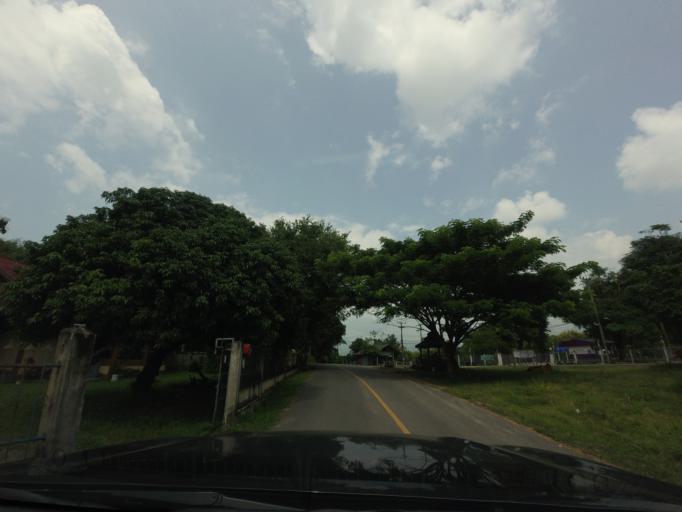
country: TH
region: Nan
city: Pua
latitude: 19.1676
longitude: 100.9270
